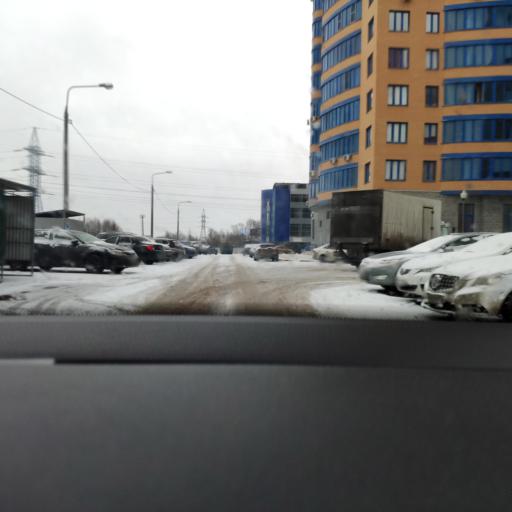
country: RU
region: Moscow
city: Ivanovskoye
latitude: 55.7753
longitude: 37.8475
